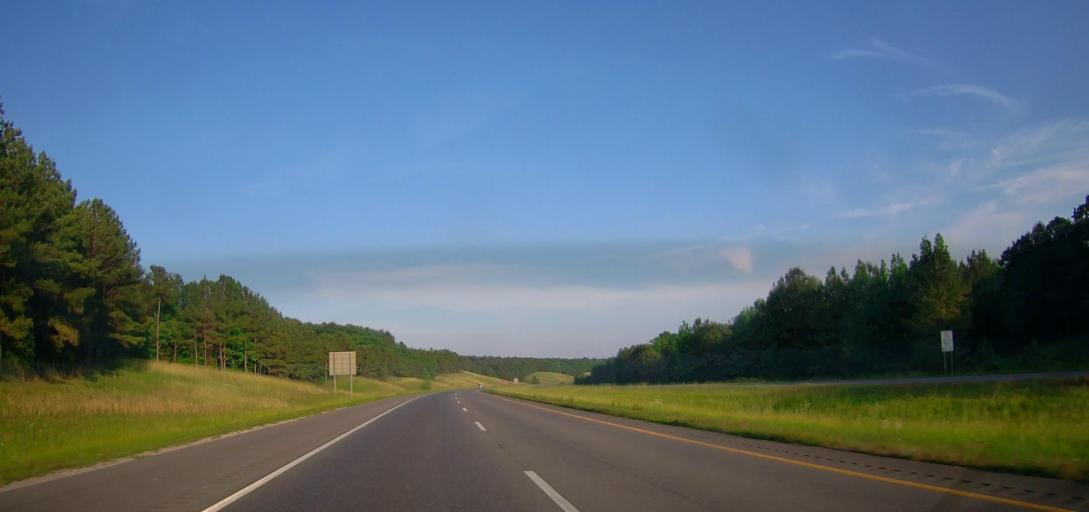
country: US
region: Alabama
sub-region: Marion County
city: Hamilton
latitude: 34.1137
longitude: -88.0298
